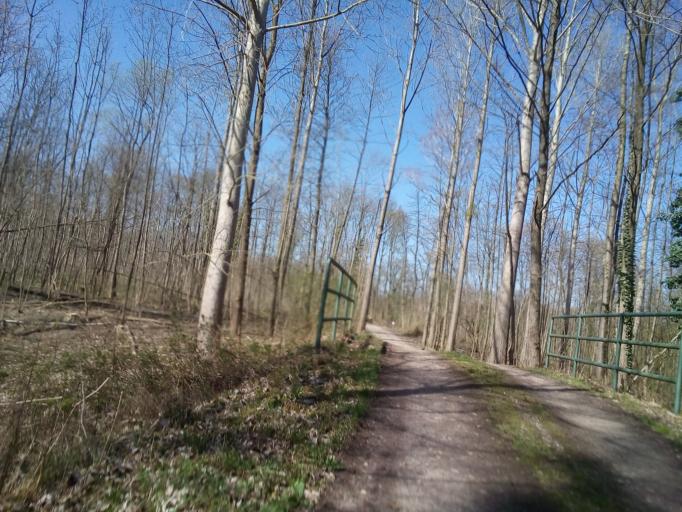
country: DE
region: Baden-Wuerttemberg
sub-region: Freiburg Region
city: Rheinau
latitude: 48.6641
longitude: 7.9035
